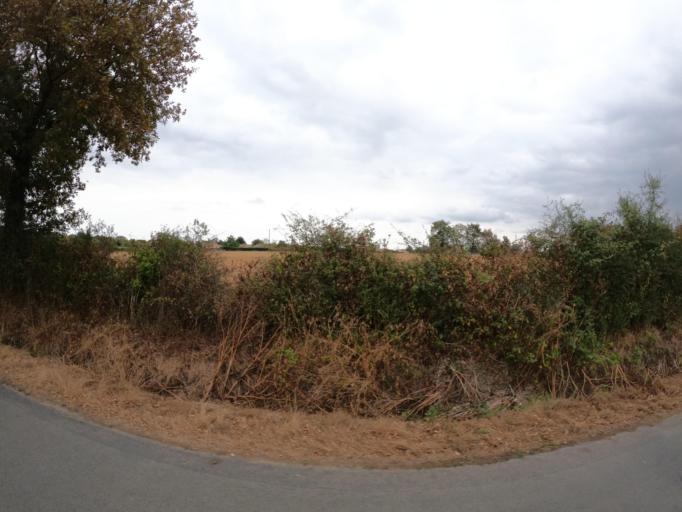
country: FR
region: Pays de la Loire
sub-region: Departement de la Vendee
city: La Boissiere-de-Montaigu
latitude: 46.9780
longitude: -1.1769
